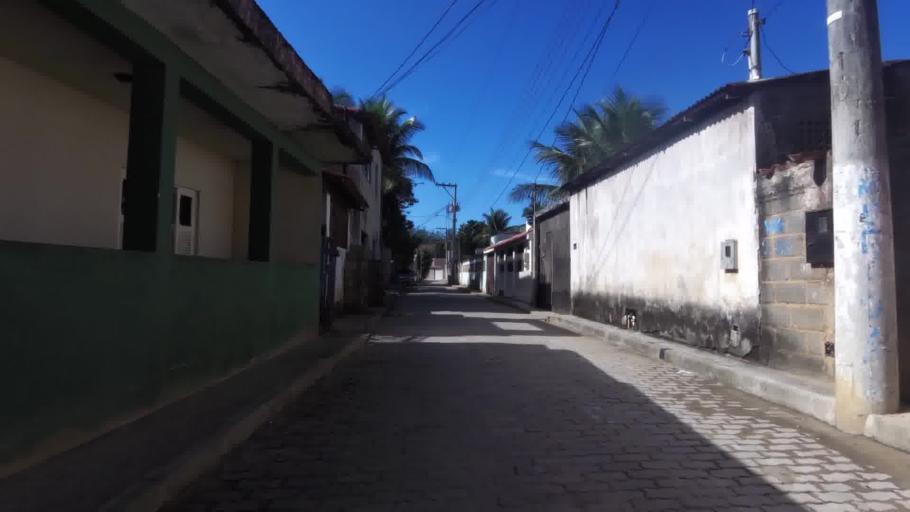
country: BR
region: Espirito Santo
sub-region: Piuma
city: Piuma
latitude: -20.8142
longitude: -40.6325
